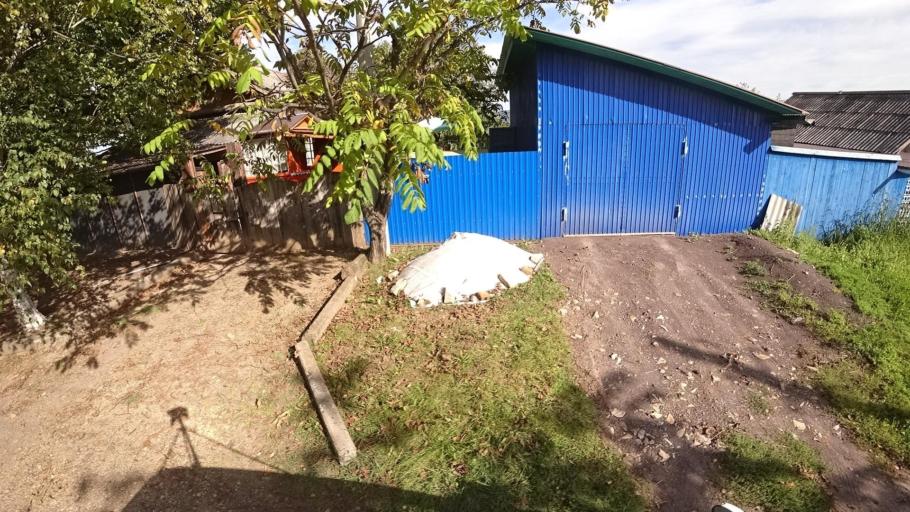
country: RU
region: Primorskiy
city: Dostoyevka
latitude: 44.3066
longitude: 133.4487
